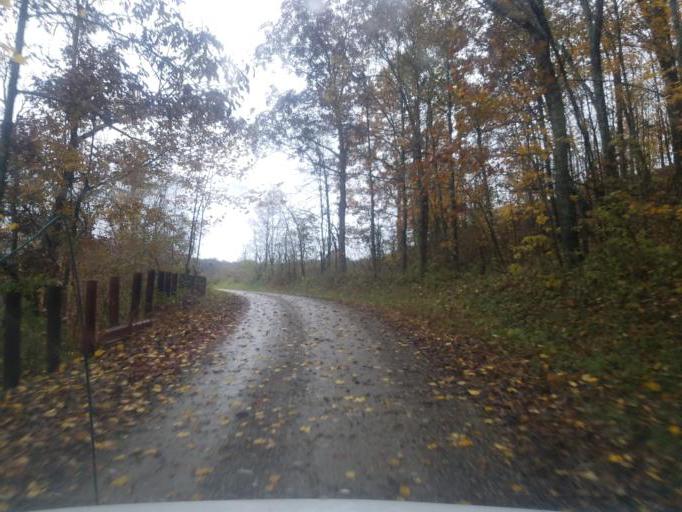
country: US
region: Ohio
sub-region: Washington County
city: Beverly
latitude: 39.4599
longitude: -81.7805
